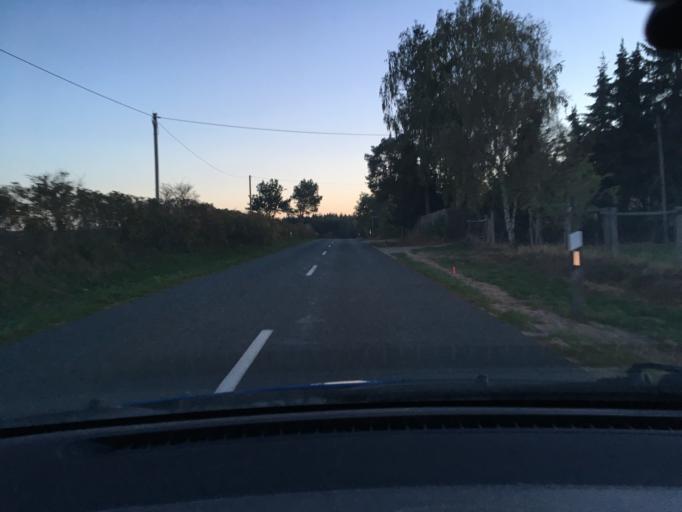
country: DE
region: Lower Saxony
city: Reinstorf
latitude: 53.2271
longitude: 10.5707
